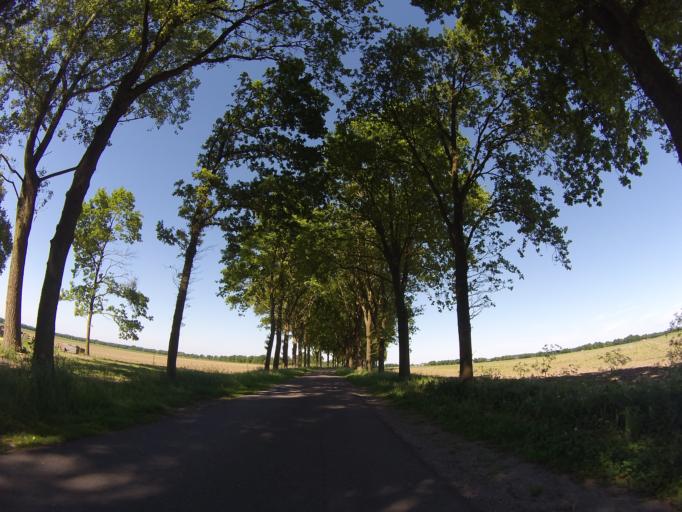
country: NL
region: Drenthe
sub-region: Gemeente Coevorden
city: Sleen
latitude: 52.7807
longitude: 6.7882
